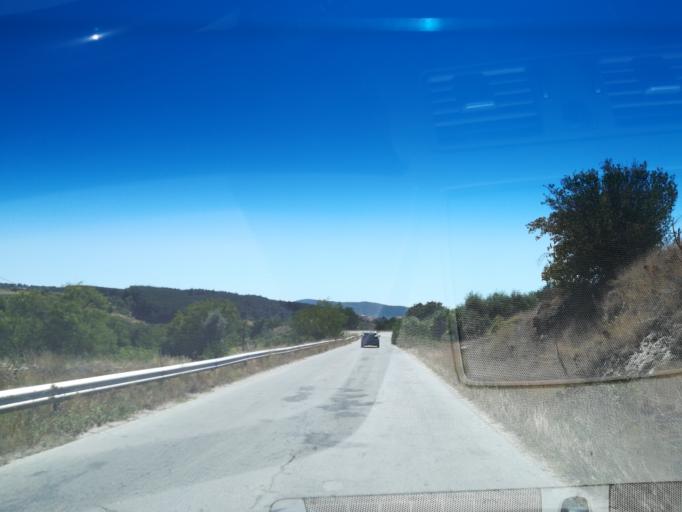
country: BG
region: Pazardzhik
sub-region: Obshtina Strelcha
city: Strelcha
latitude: 42.5196
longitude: 24.3220
